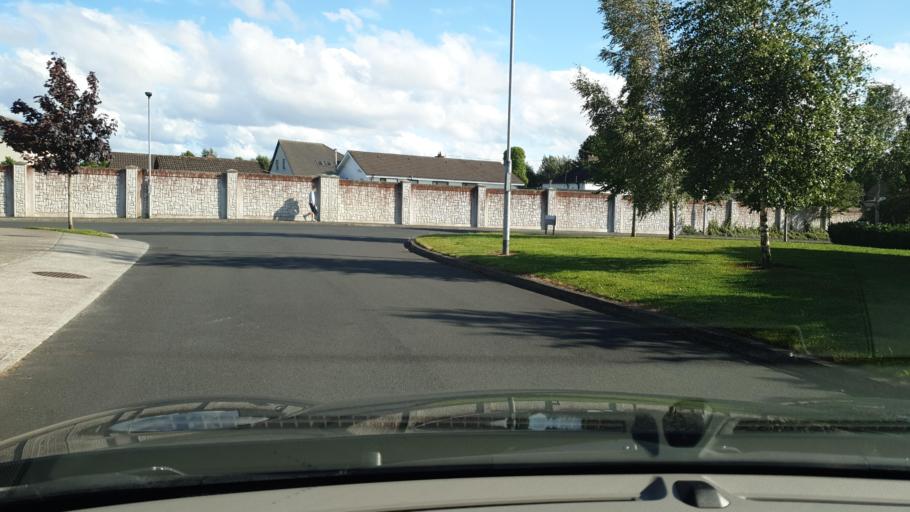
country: IE
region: Leinster
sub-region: An Mhi
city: Ashbourne
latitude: 53.5088
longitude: -6.3884
